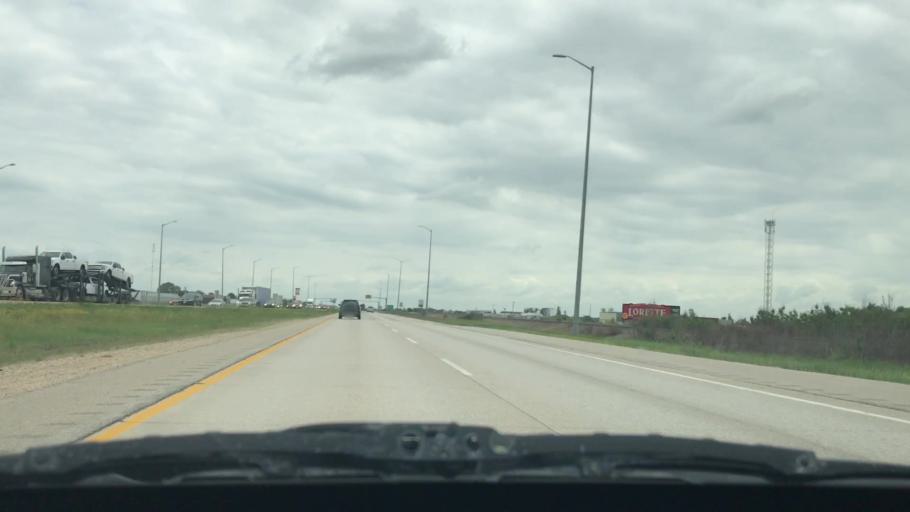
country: CA
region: Manitoba
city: Winnipeg
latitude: 49.8231
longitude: -96.9432
